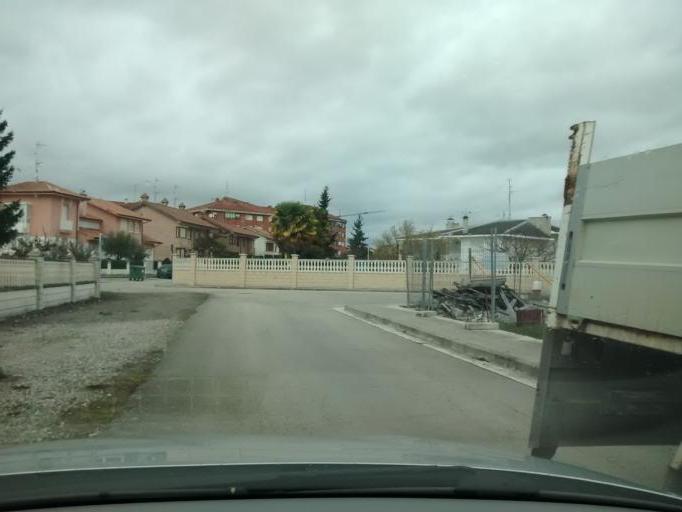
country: ES
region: Castille and Leon
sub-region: Provincia de Burgos
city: Medina de Pomar
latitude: 42.9367
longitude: -3.4828
